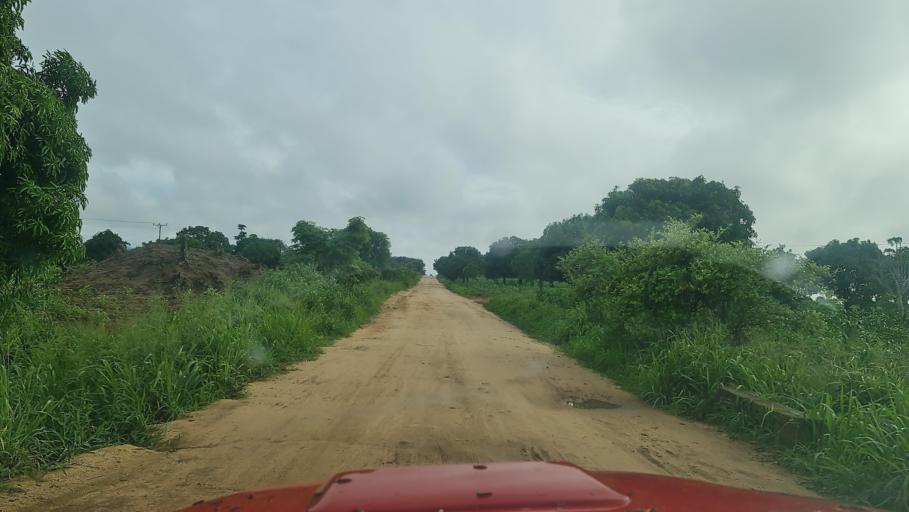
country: MW
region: Southern Region
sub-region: Nsanje District
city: Nsanje
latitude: -17.2904
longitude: 35.6023
